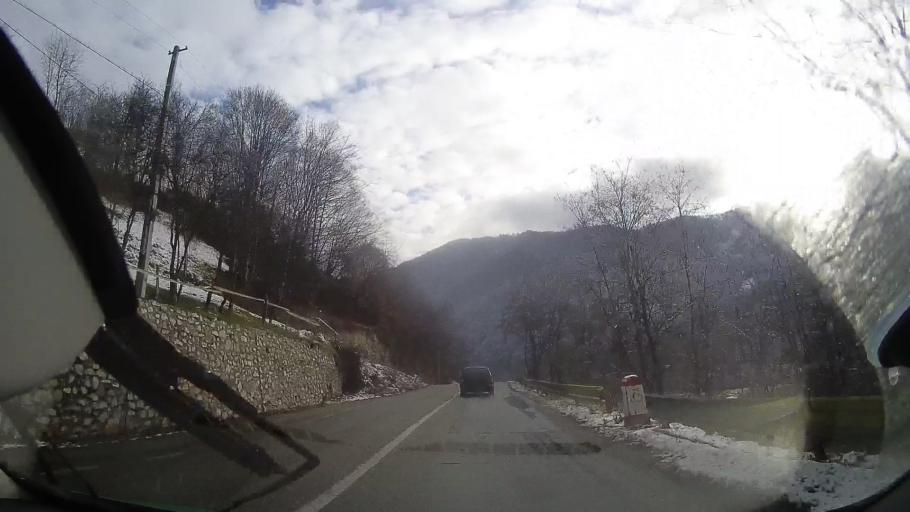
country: RO
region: Alba
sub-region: Oras Baia de Aries
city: Baia de Aries
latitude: 46.3996
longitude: 23.3106
